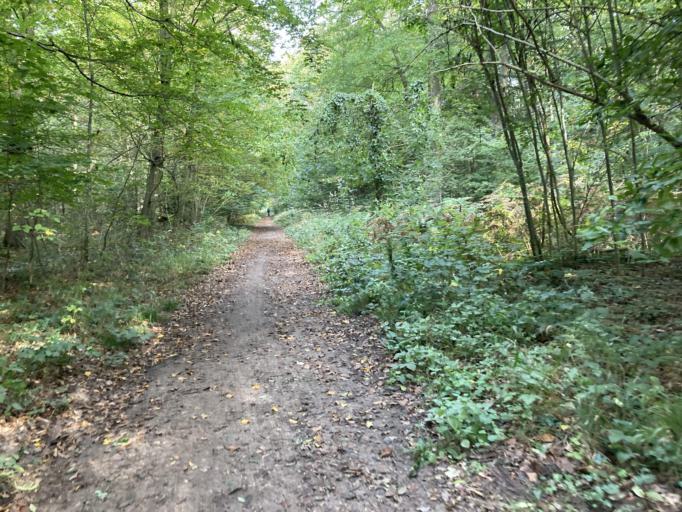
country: FR
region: Ile-de-France
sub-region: Departement des Yvelines
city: Saint-Germain-en-Laye
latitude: 48.9236
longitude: 2.0962
